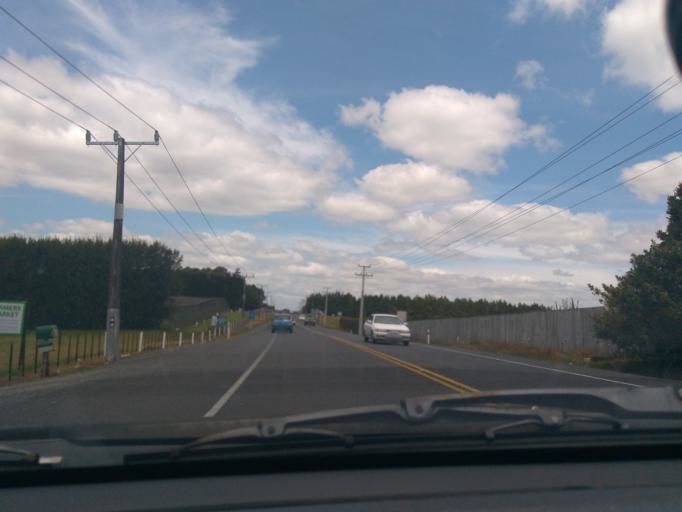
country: NZ
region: Northland
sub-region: Far North District
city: Kerikeri
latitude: -35.2029
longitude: 173.9133
